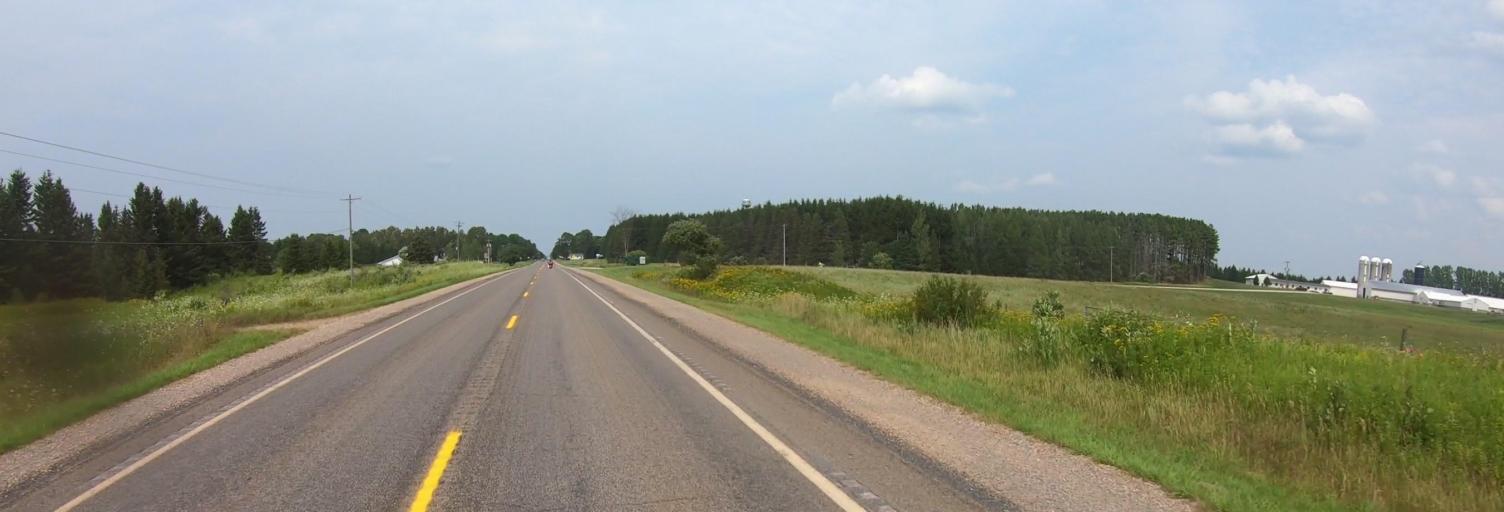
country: US
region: Michigan
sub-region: Alger County
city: Munising
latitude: 46.3389
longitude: -86.9289
